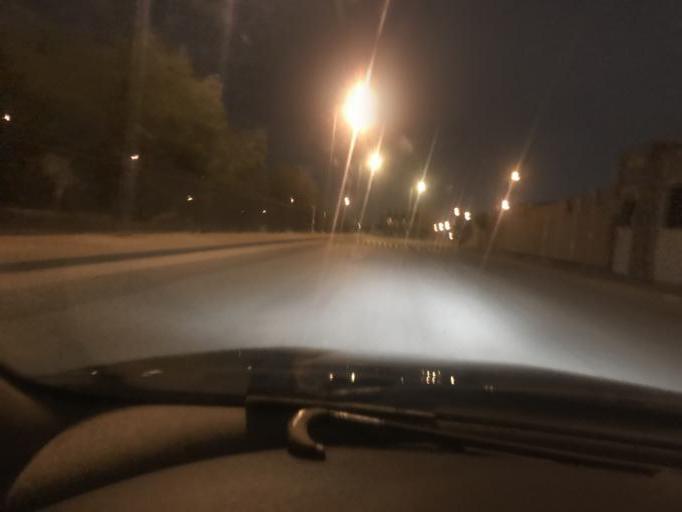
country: SA
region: Ar Riyad
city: Riyadh
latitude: 24.8071
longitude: 46.6755
